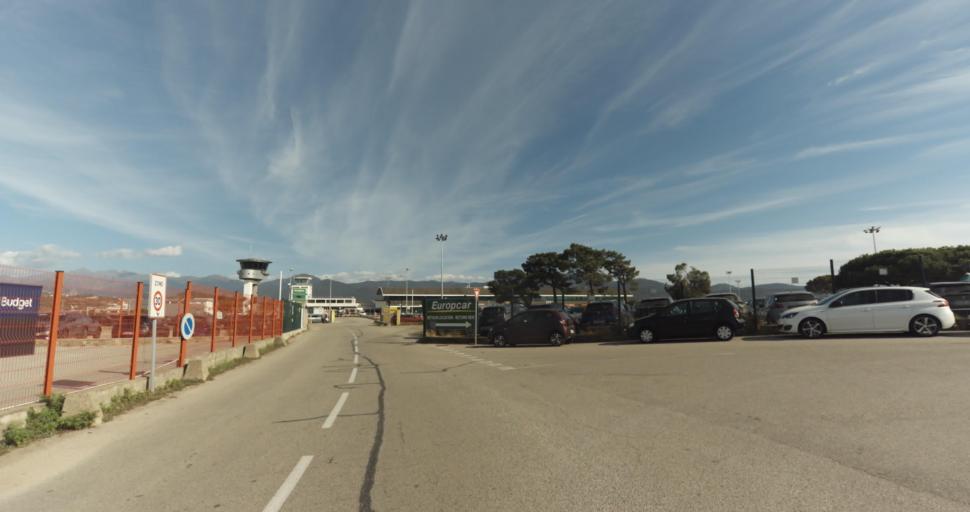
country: FR
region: Corsica
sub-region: Departement de la Corse-du-Sud
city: Ajaccio
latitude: 41.9211
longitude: 8.7920
